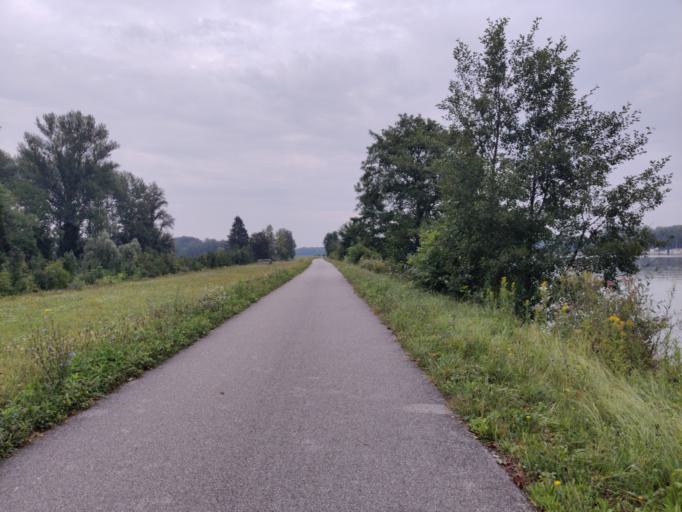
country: AT
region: Upper Austria
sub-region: Politischer Bezirk Urfahr-Umgebung
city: Steyregg
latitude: 48.2620
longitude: 14.3958
